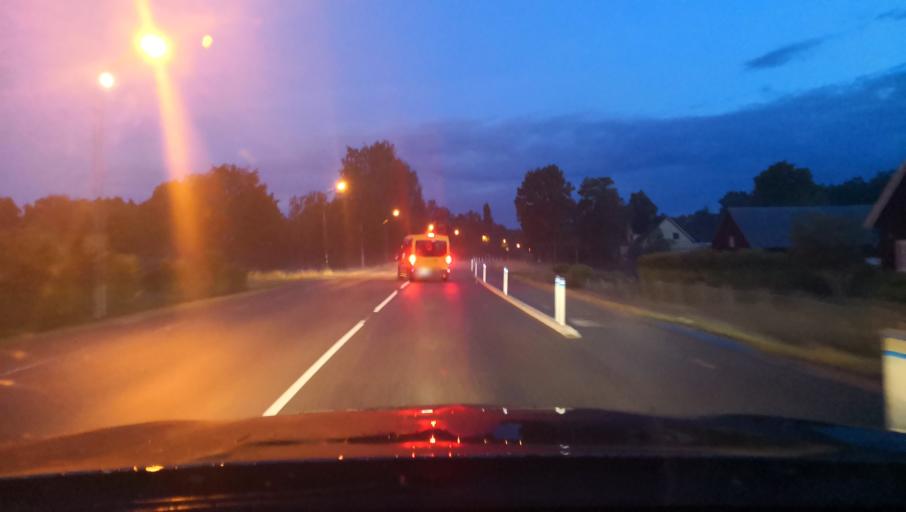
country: SE
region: Skane
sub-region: Osby Kommun
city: Osby
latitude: 56.3629
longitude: 13.9804
